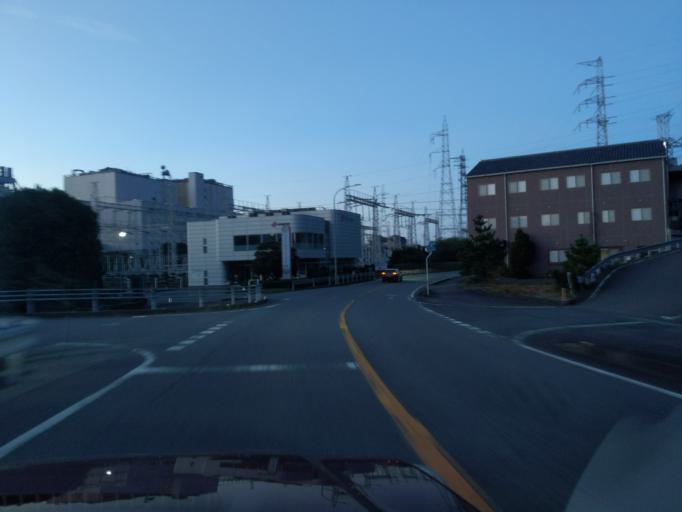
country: JP
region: Tokushima
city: Anan
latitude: 33.8811
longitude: 134.6527
